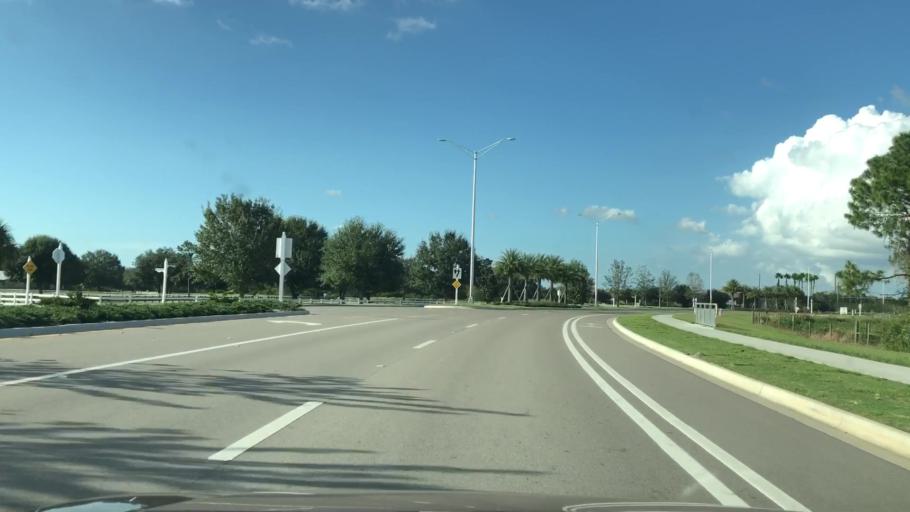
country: US
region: Florida
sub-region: Sarasota County
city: The Meadows
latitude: 27.3834
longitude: -82.3974
